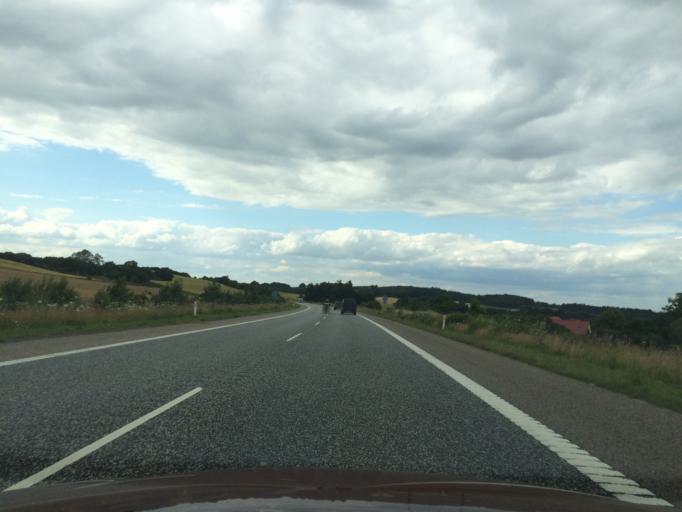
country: DK
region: Central Jutland
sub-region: Syddjurs Kommune
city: Ronde
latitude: 56.3094
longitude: 10.5008
